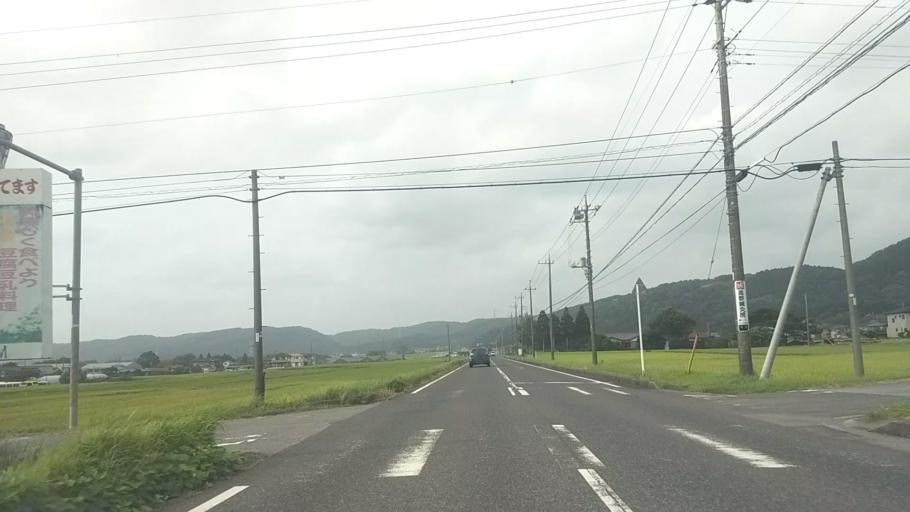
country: JP
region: Chiba
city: Kimitsu
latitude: 35.2864
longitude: 139.9902
